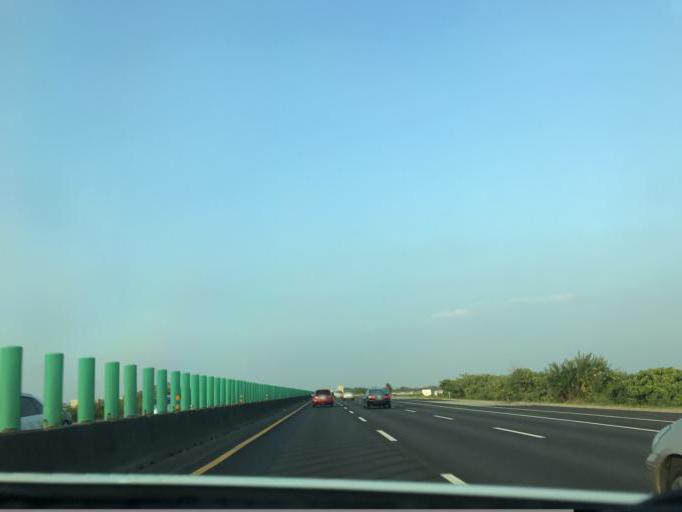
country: TW
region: Taiwan
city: Xinying
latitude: 23.2433
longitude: 120.2506
